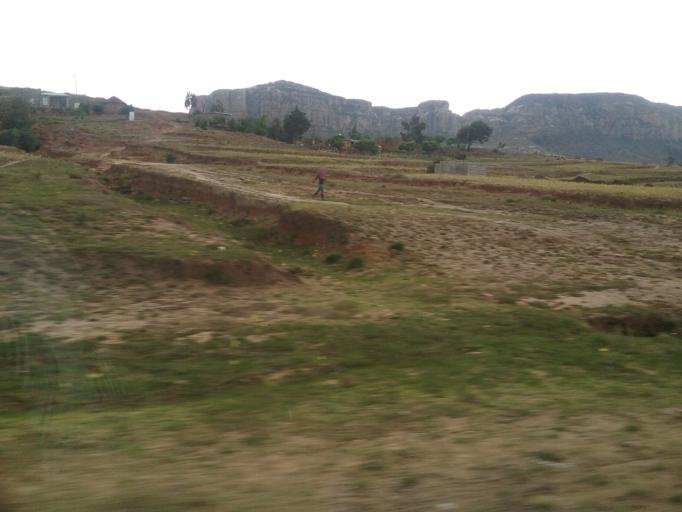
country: LS
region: Maseru
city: Nako
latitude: -29.4363
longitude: 27.6831
